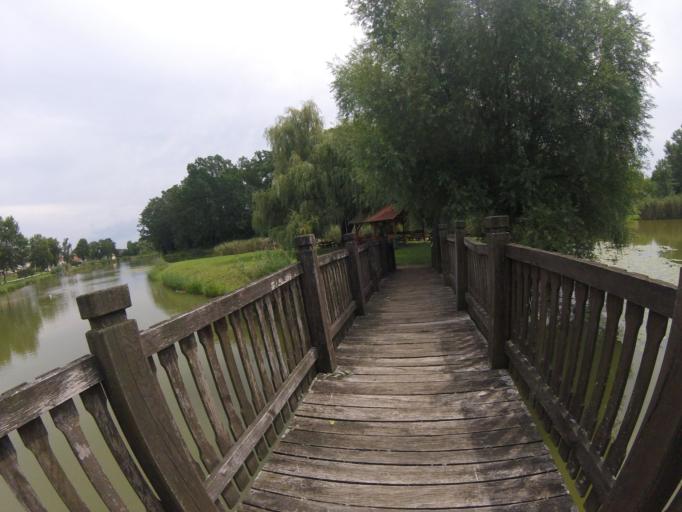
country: HR
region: Medimurska
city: Podturen
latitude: 46.5002
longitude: 16.5803
